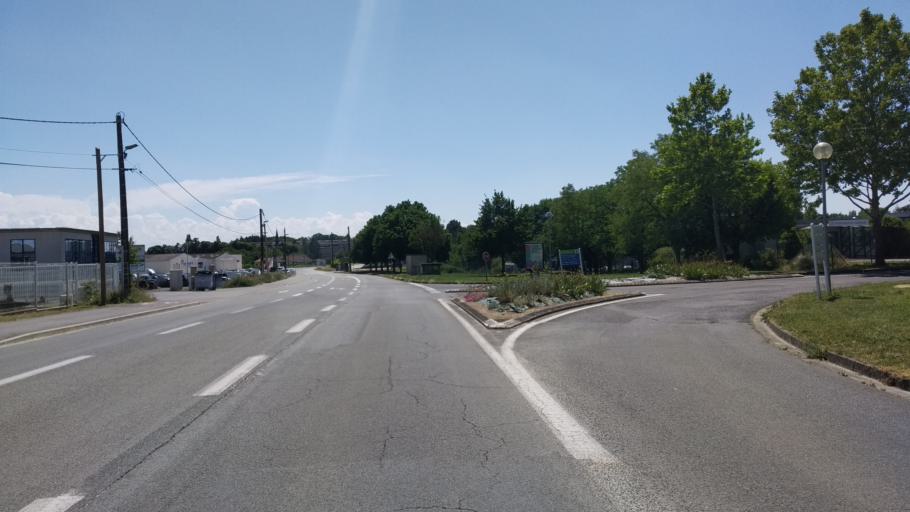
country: FR
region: Poitou-Charentes
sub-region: Departement de la Vienne
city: Biard
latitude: 46.6016
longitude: 0.3051
